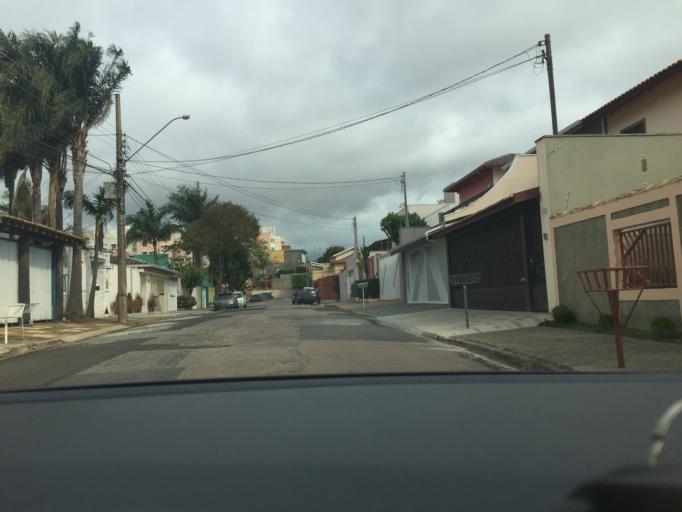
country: BR
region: Sao Paulo
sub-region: Jundiai
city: Jundiai
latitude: -23.2028
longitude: -46.8983
